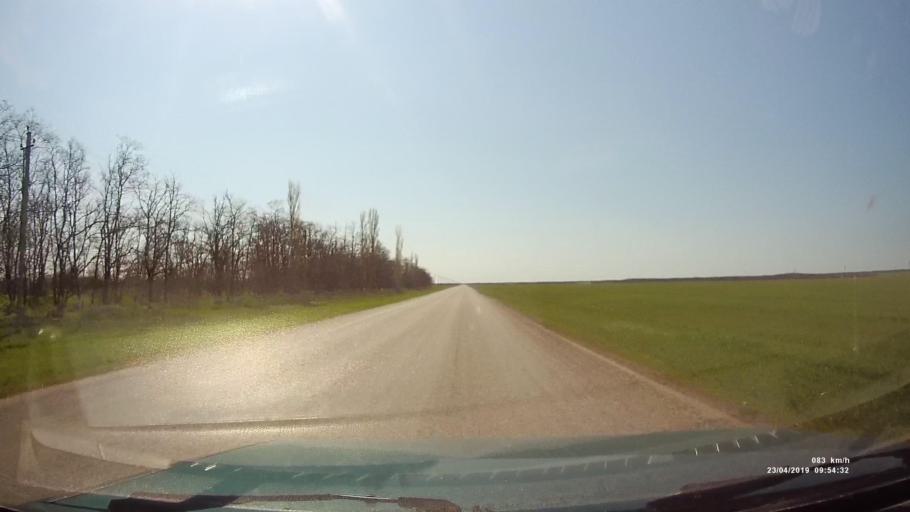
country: RU
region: Rostov
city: Orlovskiy
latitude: 46.8199
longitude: 42.0560
